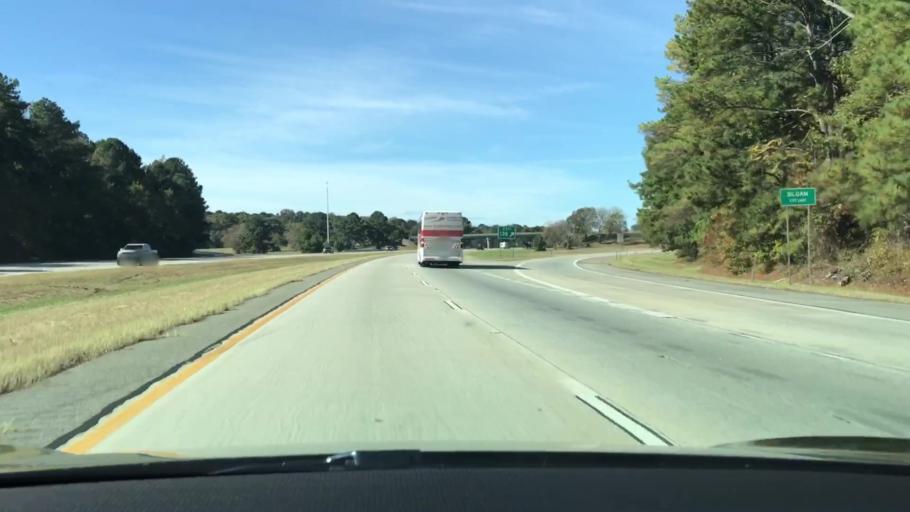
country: US
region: Georgia
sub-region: Greene County
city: Union Point
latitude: 33.5446
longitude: -83.0749
